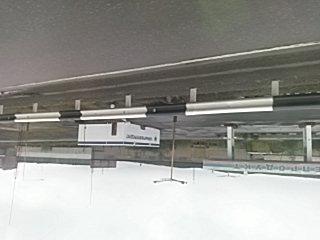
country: RU
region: Krasnoyarskiy
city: Dudinka
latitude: 69.4045
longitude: 86.2259
